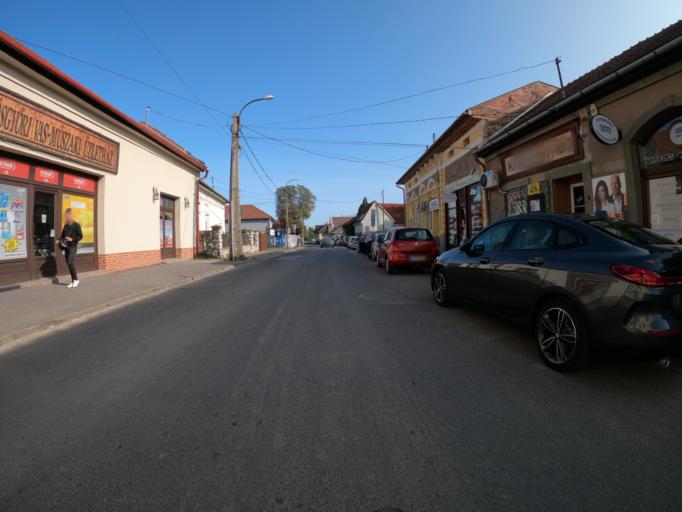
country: HU
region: Borsod-Abauj-Zemplen
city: Sajobabony
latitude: 48.1013
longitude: 20.6872
